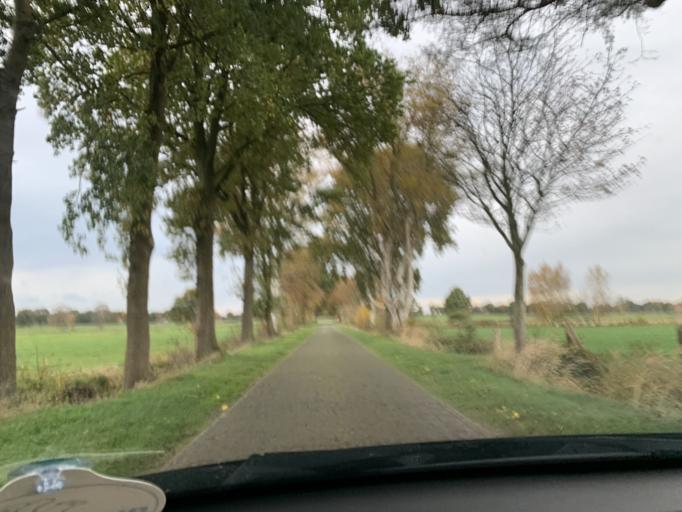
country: DE
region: Lower Saxony
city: Wiefelstede
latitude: 53.2680
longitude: 8.0492
